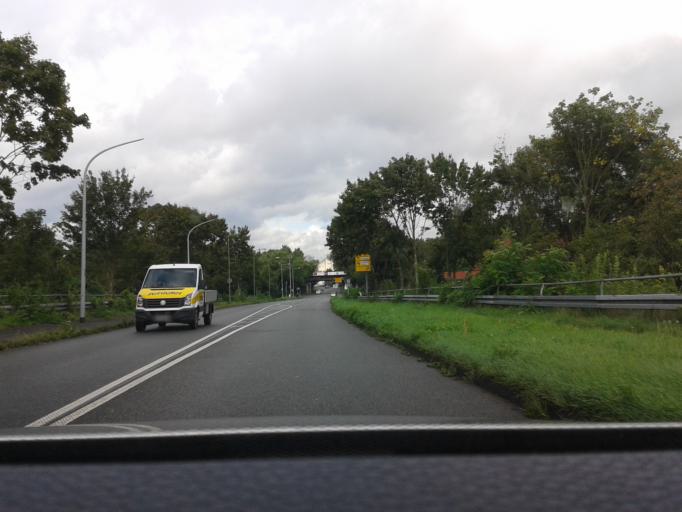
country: DE
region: North Rhine-Westphalia
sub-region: Regierungsbezirk Dusseldorf
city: Duisburg
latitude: 51.4130
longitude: 6.7954
